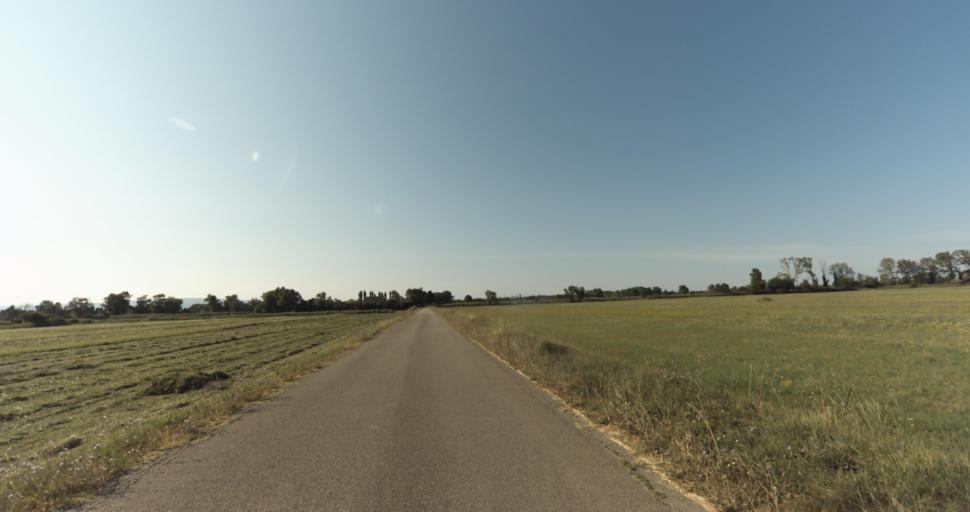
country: FR
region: Provence-Alpes-Cote d'Azur
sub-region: Departement du Vaucluse
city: Sarrians
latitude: 44.0500
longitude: 4.9505
